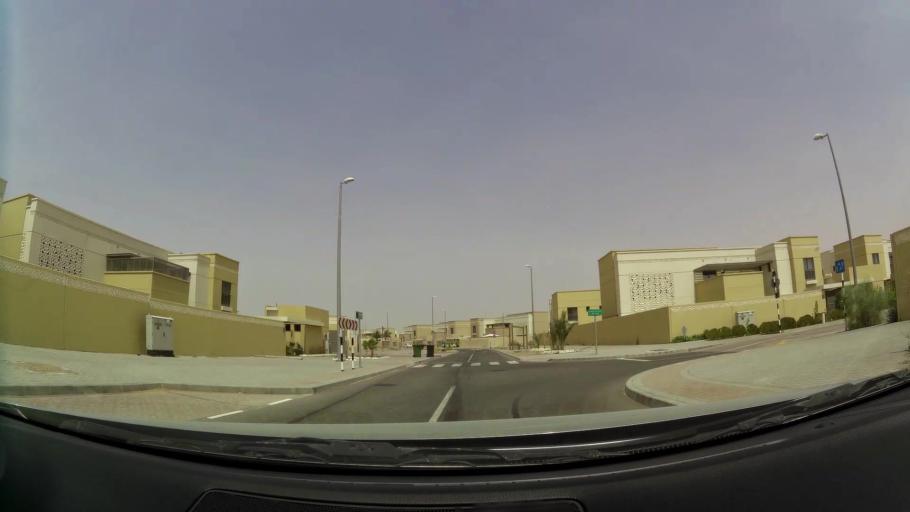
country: AE
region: Abu Dhabi
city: Al Ain
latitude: 24.1430
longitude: 55.6217
